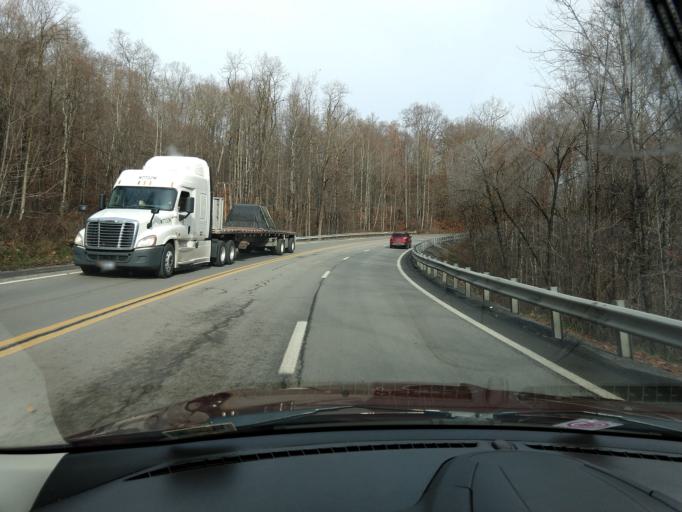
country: US
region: West Virginia
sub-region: Greenbrier County
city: Rainelle
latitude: 38.0208
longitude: -80.7254
